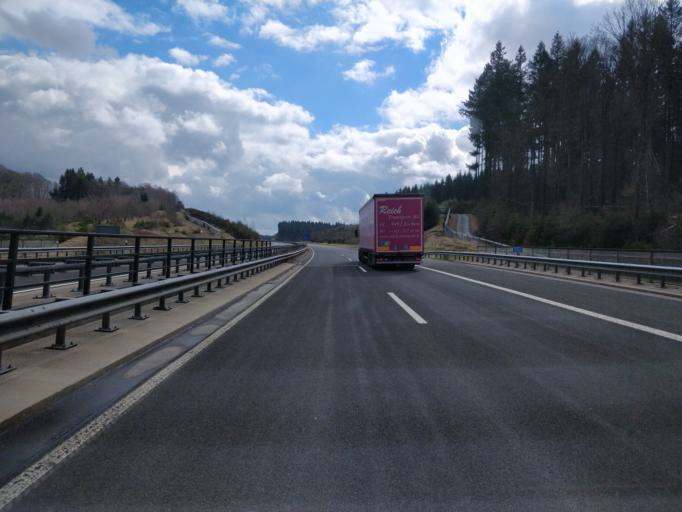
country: DE
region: Rheinland-Pfalz
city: Horscheid
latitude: 50.2126
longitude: 6.8688
